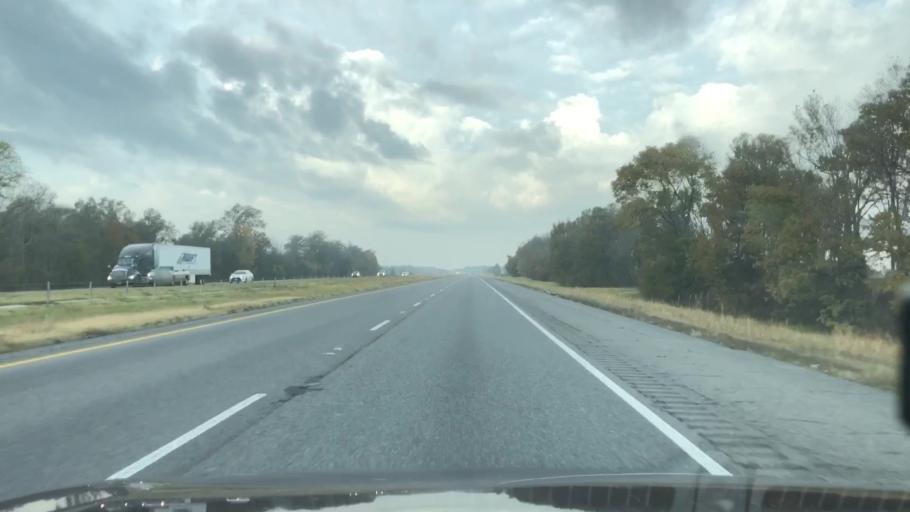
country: US
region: Louisiana
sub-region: Madison Parish
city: Tallulah
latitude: 32.4136
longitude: -91.2678
